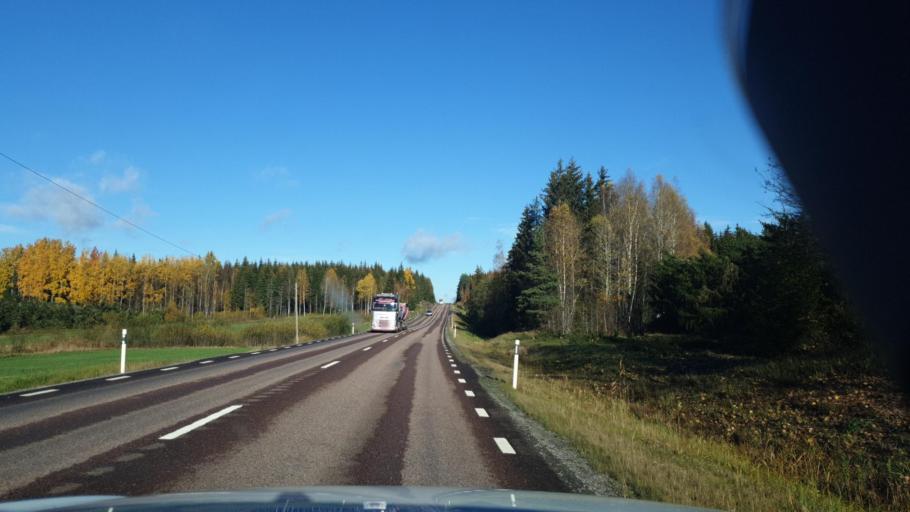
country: SE
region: Vaermland
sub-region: Sunne Kommun
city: Sunne
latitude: 59.6349
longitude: 12.9472
